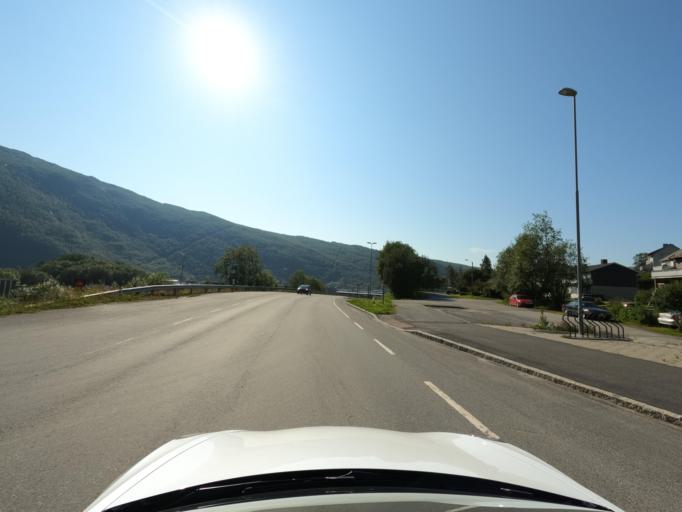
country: NO
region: Nordland
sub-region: Narvik
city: Narvik
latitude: 68.4121
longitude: 17.4353
